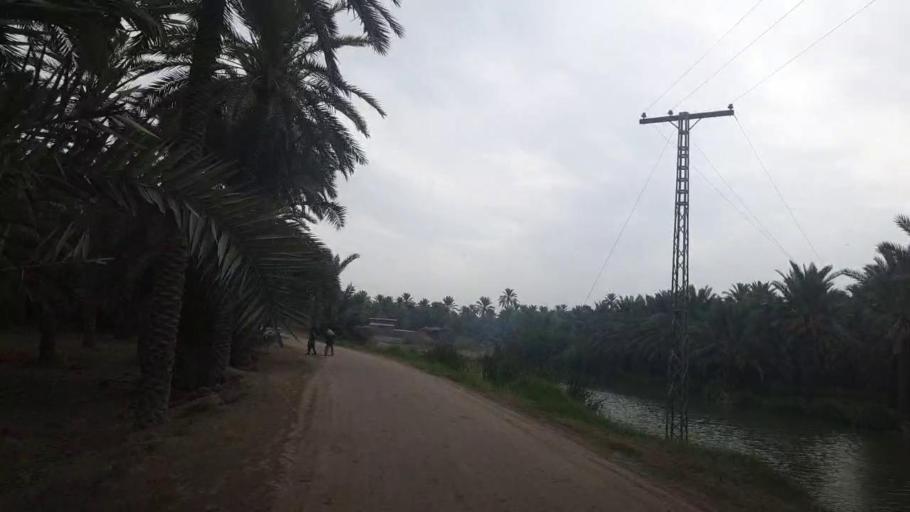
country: PK
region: Sindh
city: Khairpur
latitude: 27.5748
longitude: 68.7448
